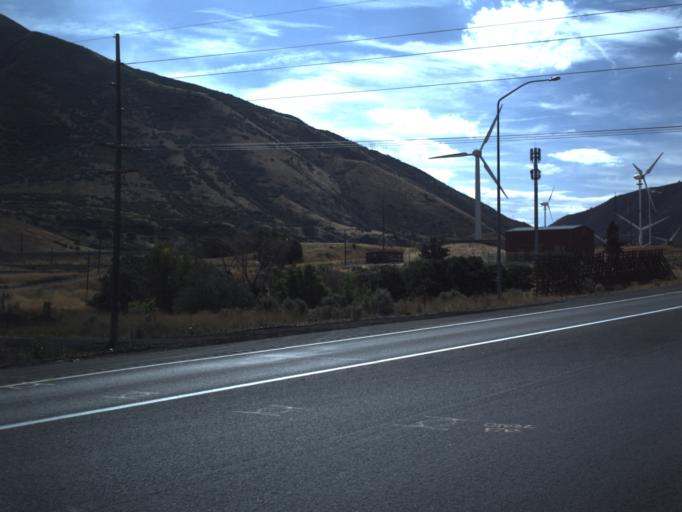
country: US
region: Utah
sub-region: Utah County
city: Mapleton
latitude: 40.0863
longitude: -111.5929
